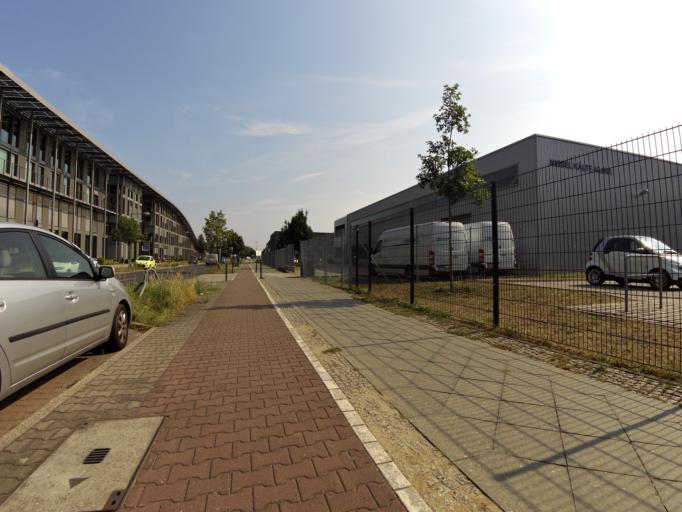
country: DE
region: Berlin
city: Adlershof
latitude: 52.4279
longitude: 13.5441
